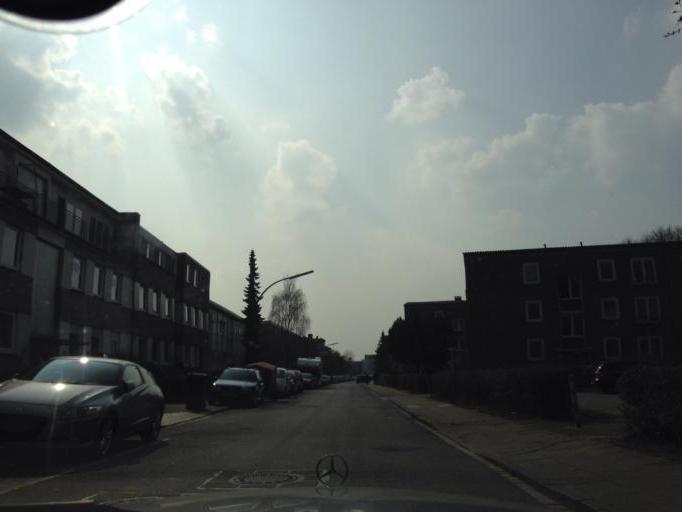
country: DE
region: Hamburg
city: Marienthal
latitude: 53.5818
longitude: 10.0847
